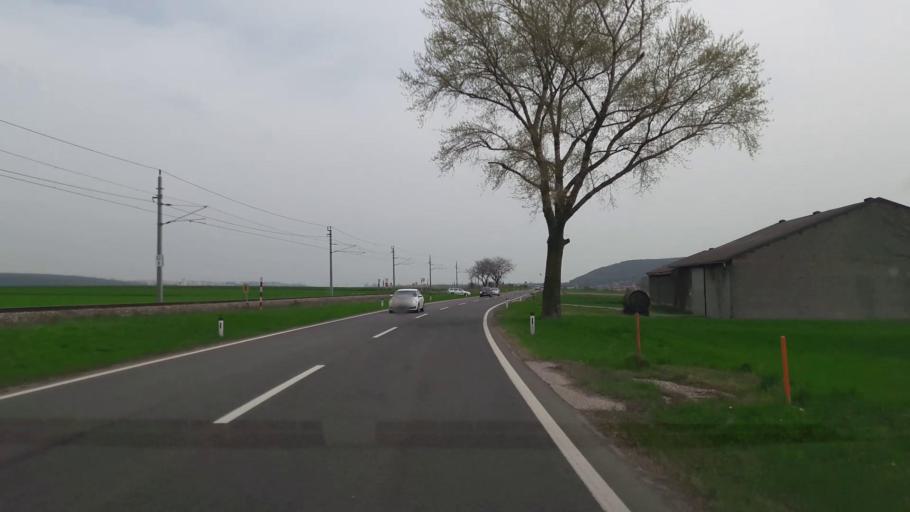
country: AT
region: Lower Austria
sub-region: Politischer Bezirk Bruck an der Leitha
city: Hainburg an der Donau
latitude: 48.1459
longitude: 16.9645
